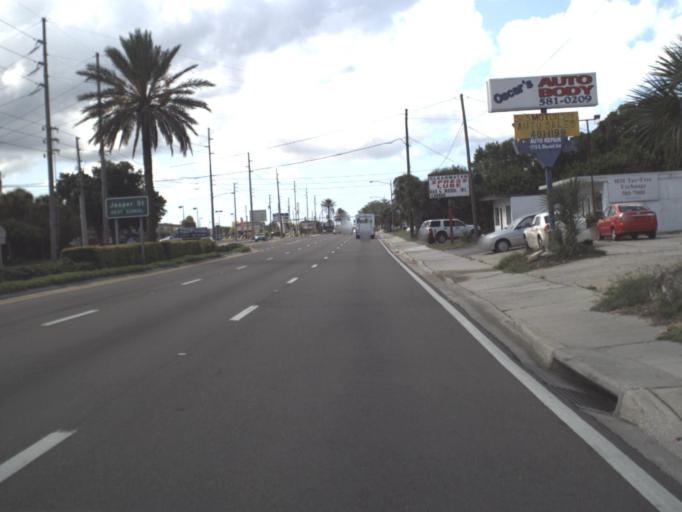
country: US
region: Florida
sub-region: Pinellas County
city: Belleair
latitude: 27.9347
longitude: -82.7876
